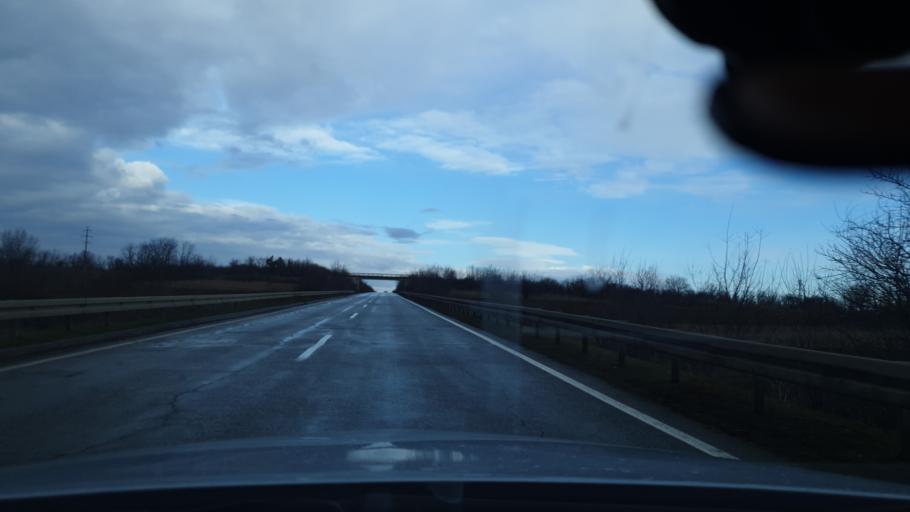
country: RS
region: Central Serbia
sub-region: Podunavski Okrug
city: Smederevo
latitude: 44.5950
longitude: 20.9565
